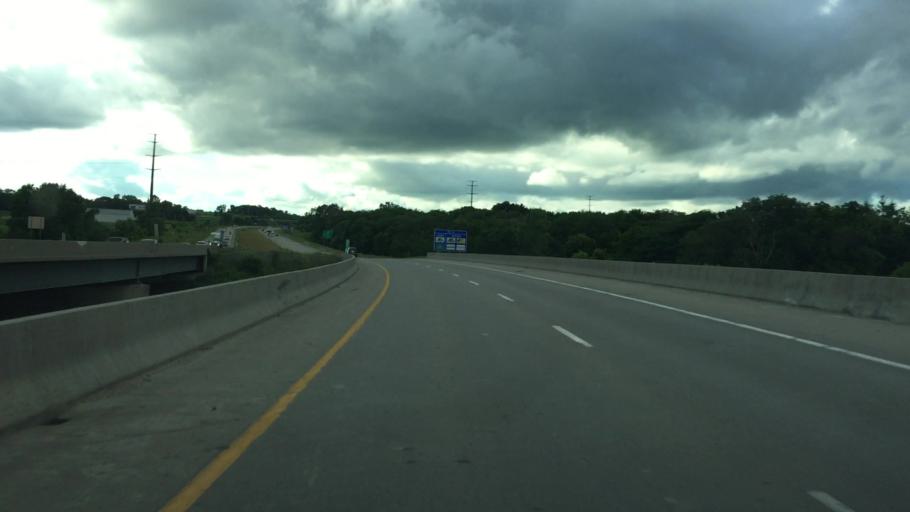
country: US
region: Iowa
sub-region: Polk County
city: Altoona
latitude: 41.6233
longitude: -93.4940
